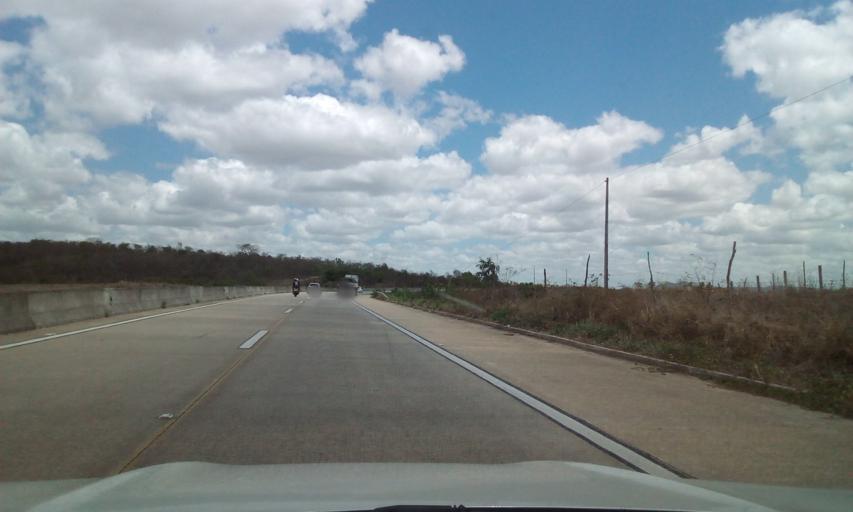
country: BR
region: Alagoas
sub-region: Porto Real Do Colegio
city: Porto Real do Colegio
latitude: -10.1555
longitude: -36.8117
